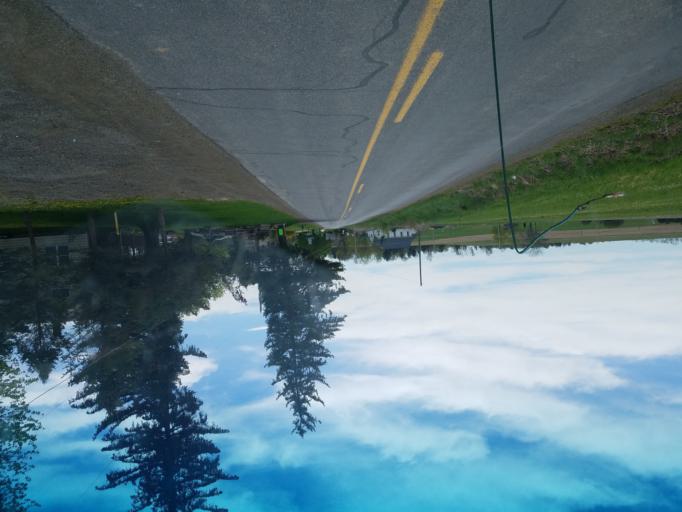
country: US
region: Pennsylvania
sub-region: Tioga County
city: Wellsboro
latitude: 41.7217
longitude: -77.3840
